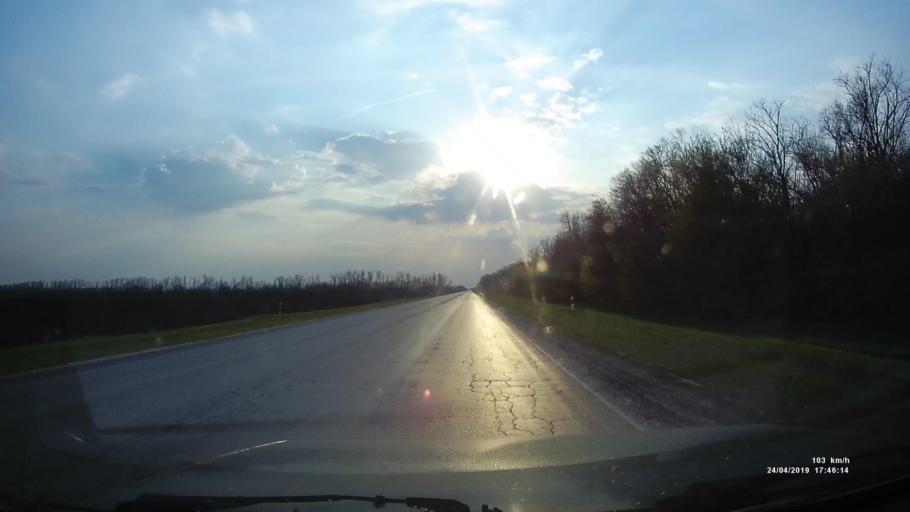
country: RU
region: Rostov
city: Tselina
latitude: 46.5373
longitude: 40.8720
